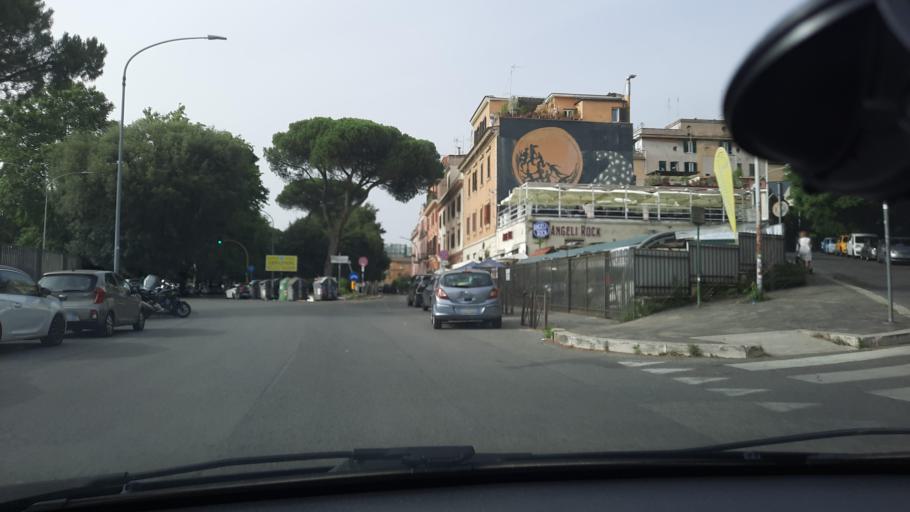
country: IT
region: Latium
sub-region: Citta metropolitana di Roma Capitale
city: Rome
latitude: 41.8599
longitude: 12.4784
